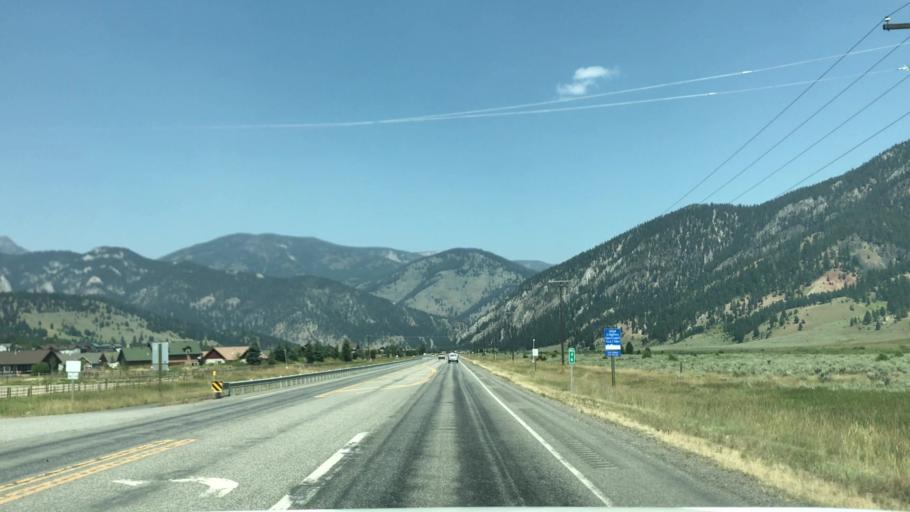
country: US
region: Montana
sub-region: Gallatin County
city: Big Sky
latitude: 45.2365
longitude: -111.2508
